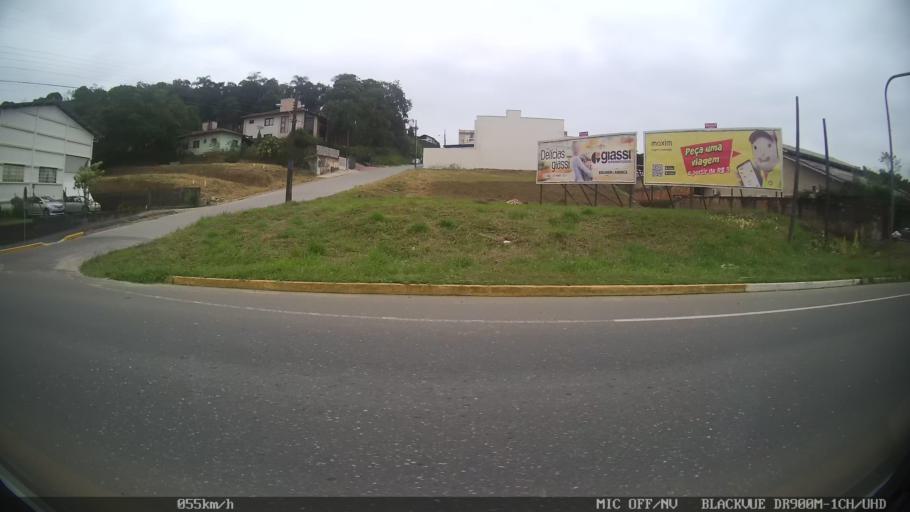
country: BR
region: Santa Catarina
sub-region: Joinville
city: Joinville
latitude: -26.3469
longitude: -48.8422
